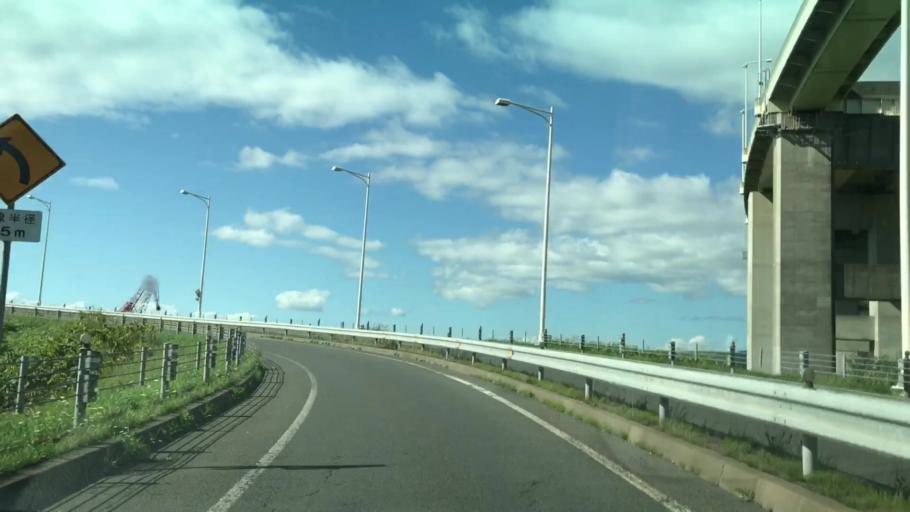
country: JP
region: Hokkaido
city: Muroran
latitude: 42.3430
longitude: 140.9492
